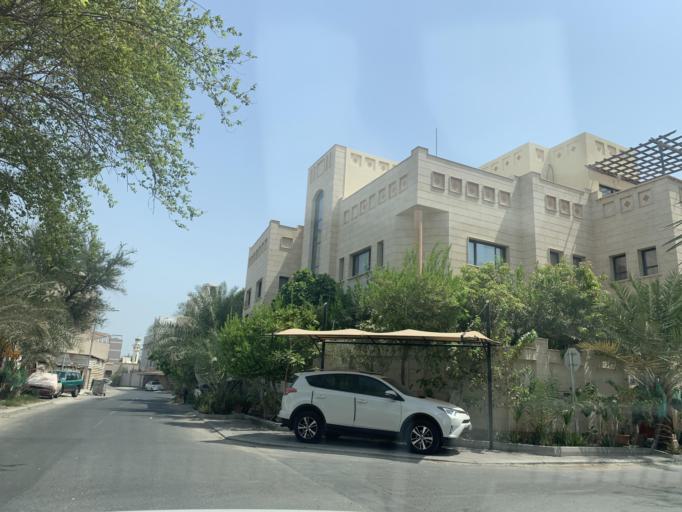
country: BH
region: Manama
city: Jidd Hafs
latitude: 26.2097
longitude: 50.5046
